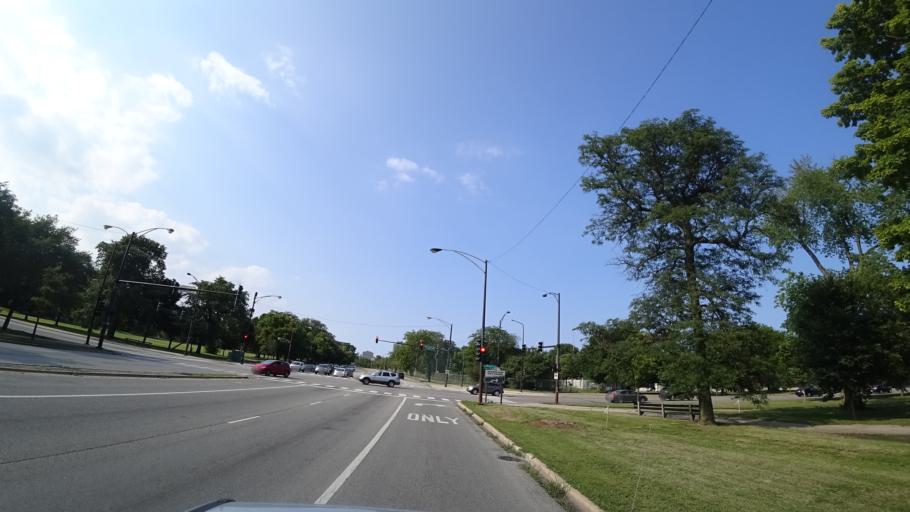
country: US
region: Illinois
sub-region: Cook County
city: Chicago
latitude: 41.7803
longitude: -87.5844
